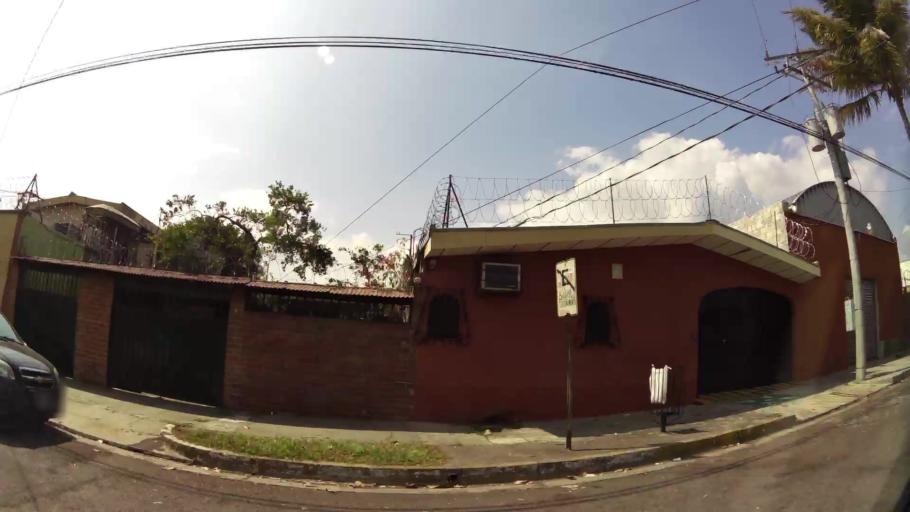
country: SV
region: San Salvador
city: Mejicanos
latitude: 13.7133
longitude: -89.2084
